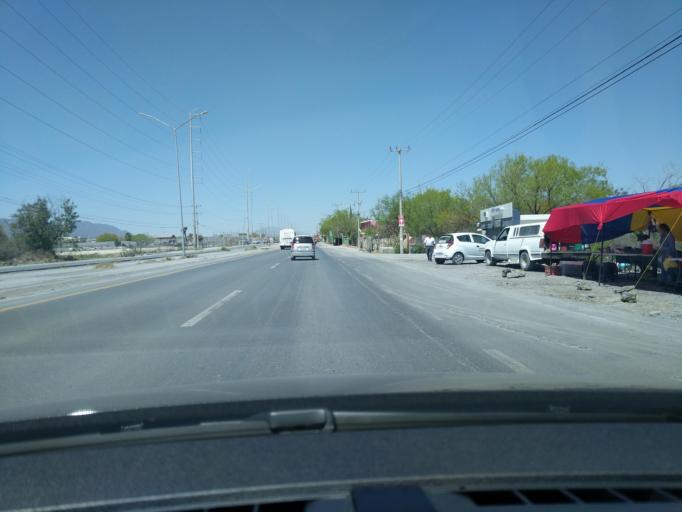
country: MX
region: Nuevo Leon
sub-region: Salinas Victoria
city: Emiliano Zapata
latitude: 25.9069
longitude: -100.2652
